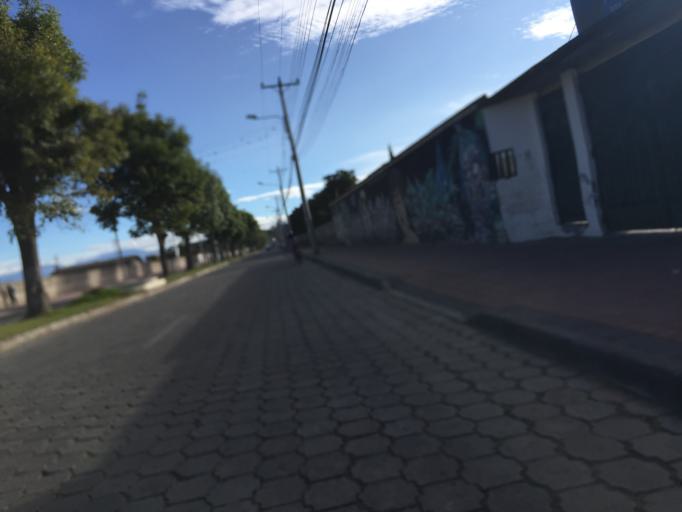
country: EC
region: Imbabura
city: Atuntaqui
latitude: 0.3359
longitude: -78.2105
